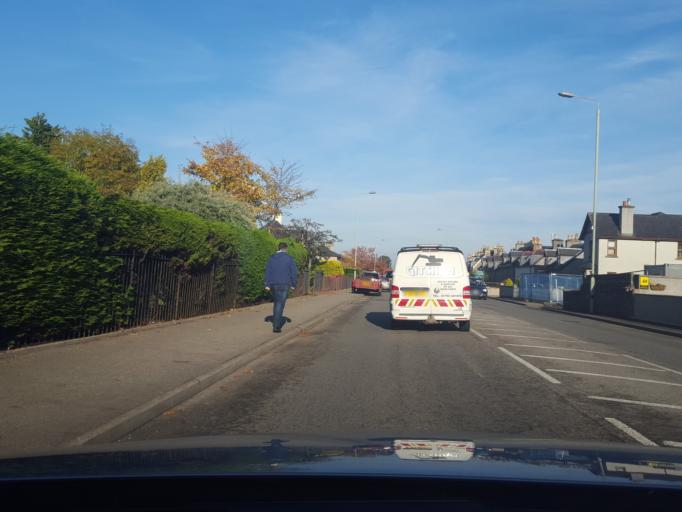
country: GB
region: Scotland
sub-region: Highland
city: Inverness
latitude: 57.4680
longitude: -4.2386
